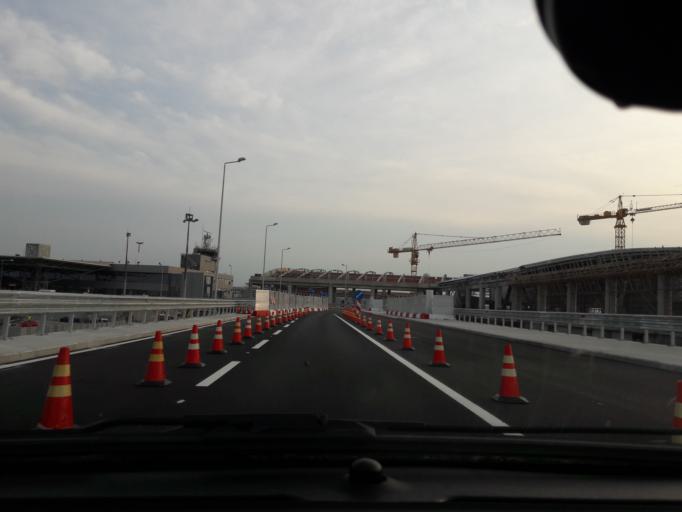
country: GR
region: Central Macedonia
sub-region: Nomos Thessalonikis
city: Neo Rysi
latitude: 40.5262
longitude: 22.9762
